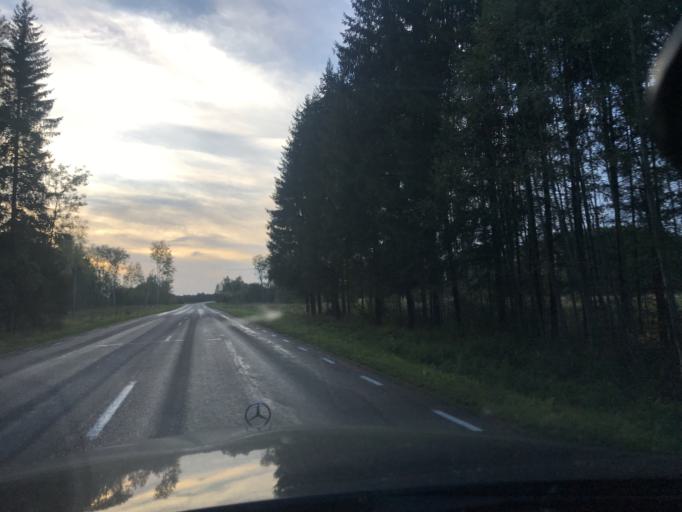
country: EE
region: Vorumaa
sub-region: Antsla vald
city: Vana-Antsla
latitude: 57.9047
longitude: 26.4385
